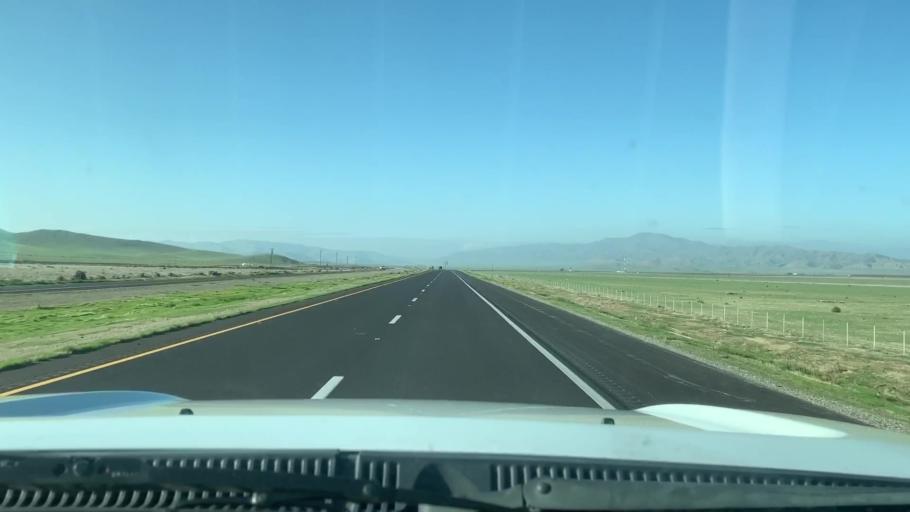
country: US
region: California
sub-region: Kern County
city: Lost Hills
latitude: 35.6431
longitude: -120.0237
